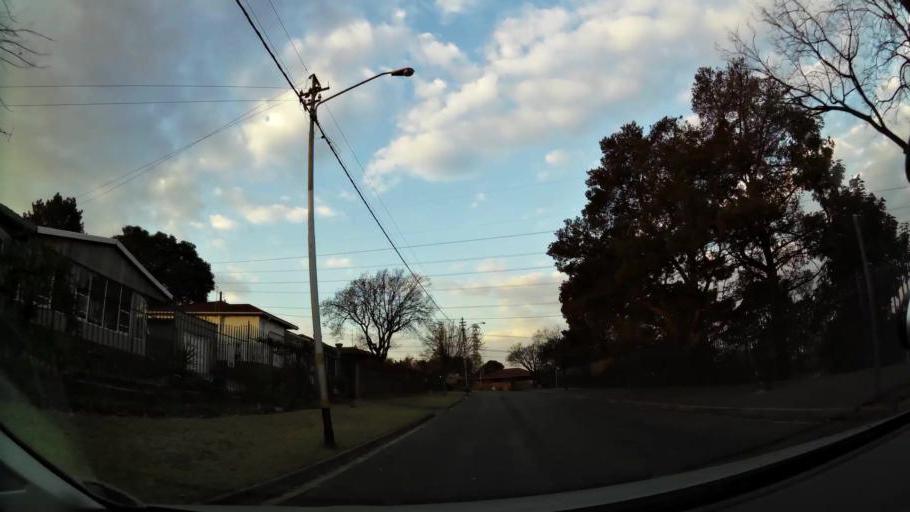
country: ZA
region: Gauteng
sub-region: Ekurhuleni Metropolitan Municipality
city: Germiston
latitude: -26.1915
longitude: 28.1444
